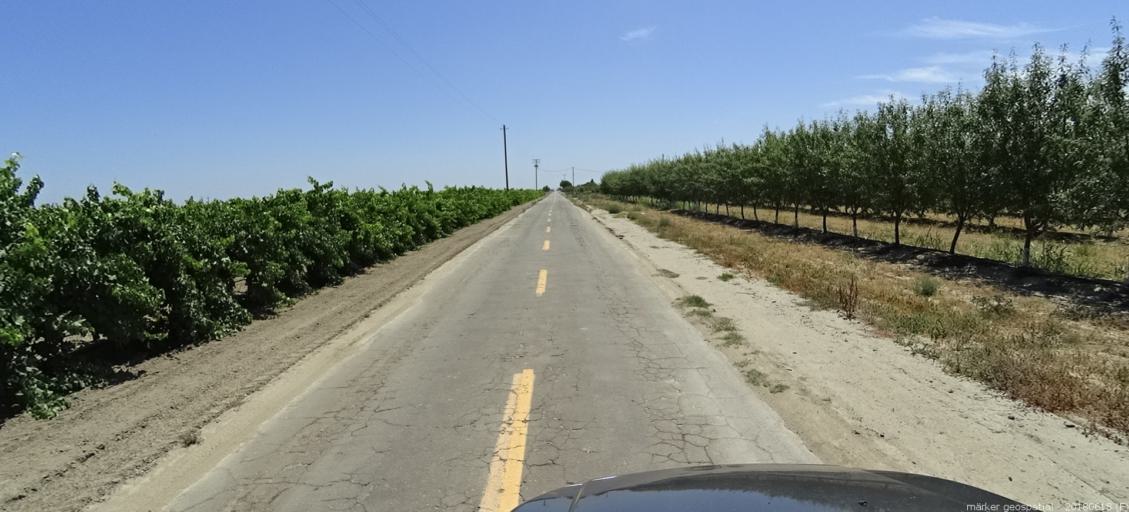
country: US
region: California
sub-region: Madera County
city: Parkwood
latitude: 36.8585
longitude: -120.1087
